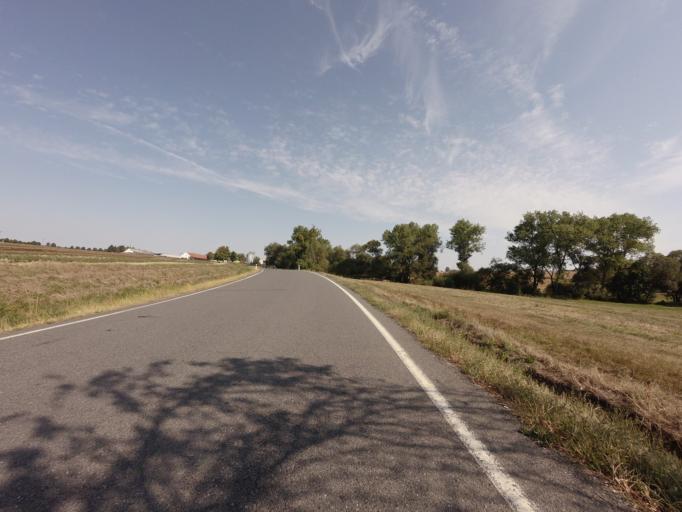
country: CZ
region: Jihocesky
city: Bernartice
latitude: 49.3597
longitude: 14.3774
